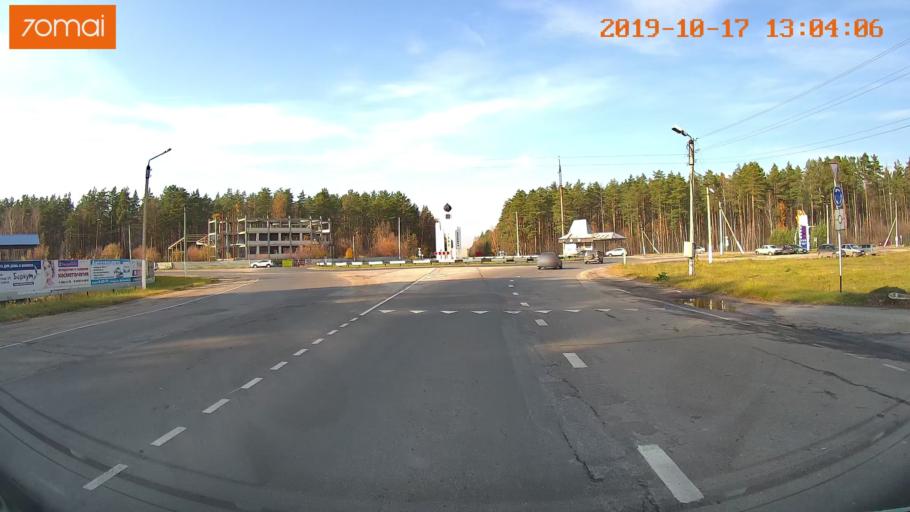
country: RU
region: Rjazan
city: Kasimov
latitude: 54.9599
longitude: 41.3466
